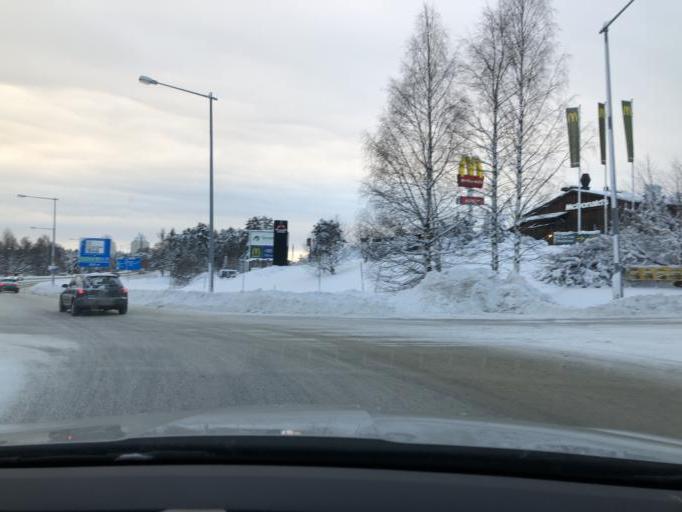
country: SE
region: Vaesterbotten
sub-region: Umea Kommun
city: Ersmark
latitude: 63.8532
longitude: 20.2973
